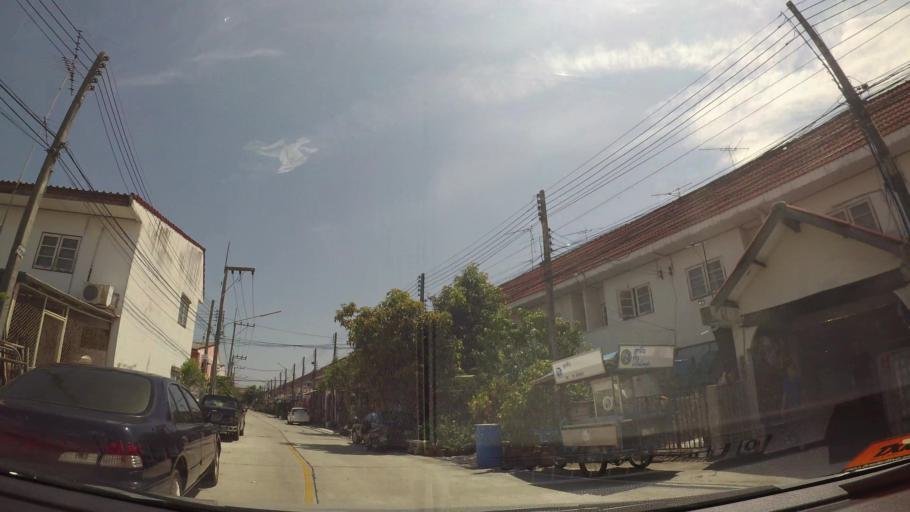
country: TH
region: Chon Buri
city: Chon Buri
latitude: 13.3280
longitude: 100.9485
